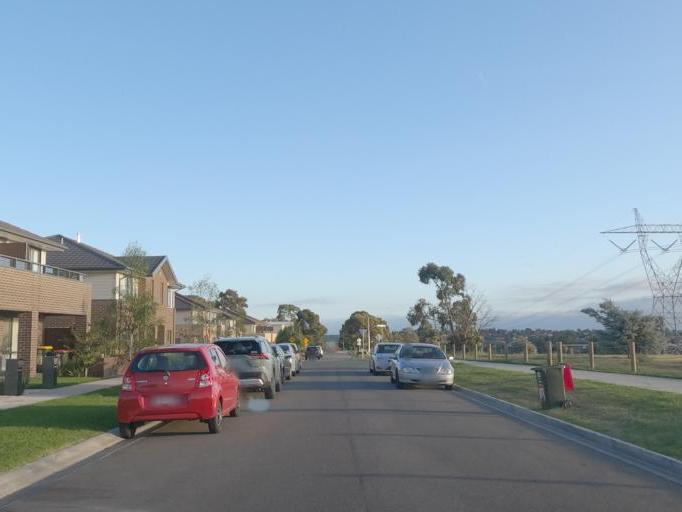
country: AU
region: Victoria
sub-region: Hume
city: Broadmeadows
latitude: -37.6721
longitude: 144.9057
